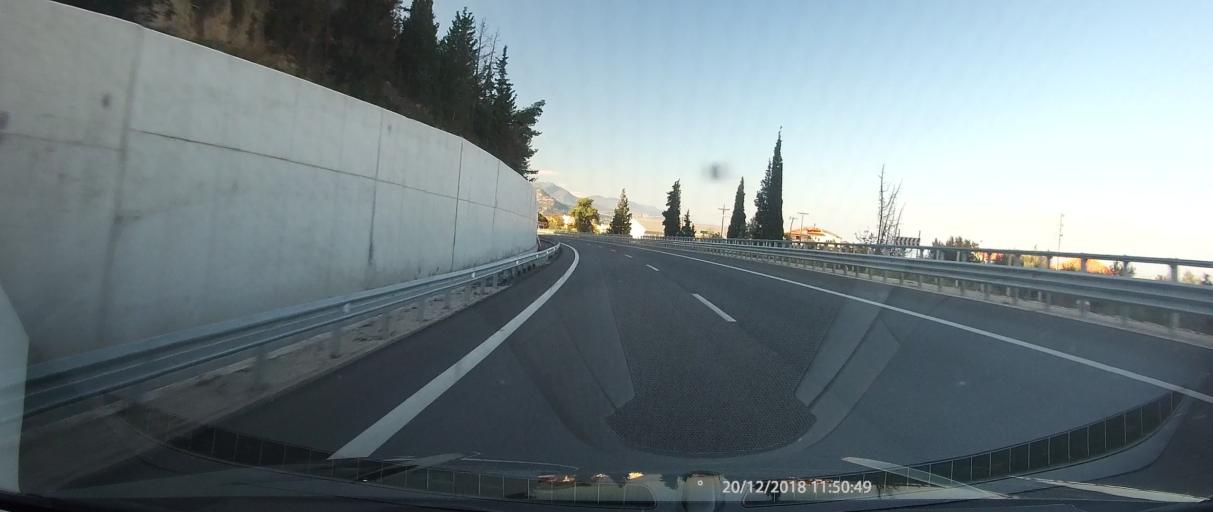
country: GR
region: West Greece
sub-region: Nomos Achaias
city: Aiyira
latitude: 38.1340
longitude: 22.4318
